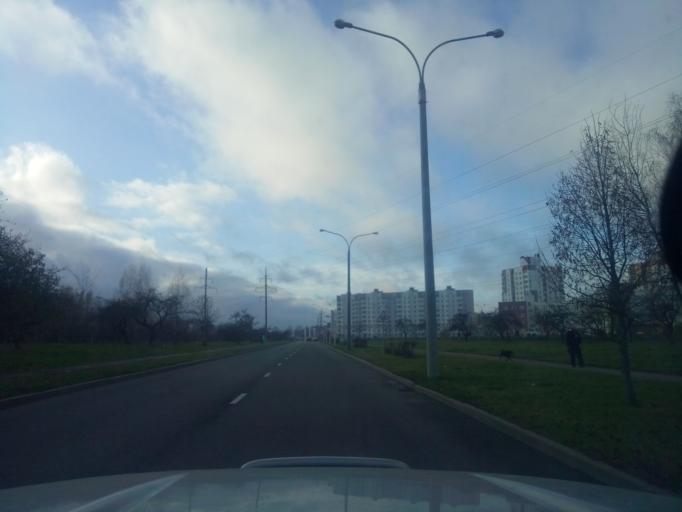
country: BY
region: Minsk
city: Novoye Medvezhino
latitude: 53.8760
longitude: 27.4906
